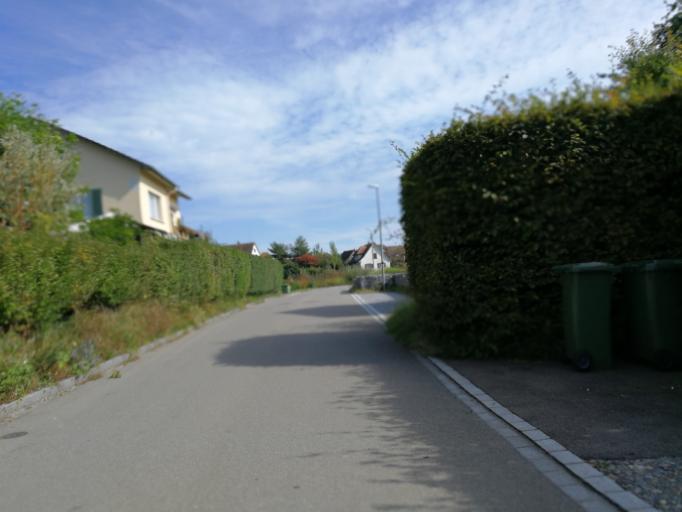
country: CH
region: Zurich
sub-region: Bezirk Meilen
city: Uetikon / Grossdorf
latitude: 47.2638
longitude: 8.6726
